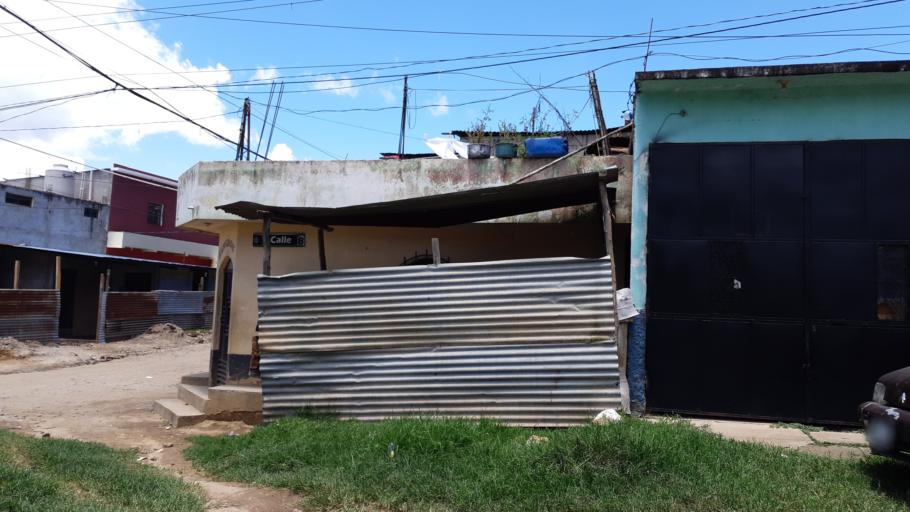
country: GT
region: Chimaltenango
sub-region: Municipio de Chimaltenango
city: Chimaltenango
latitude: 14.6651
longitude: -90.8489
